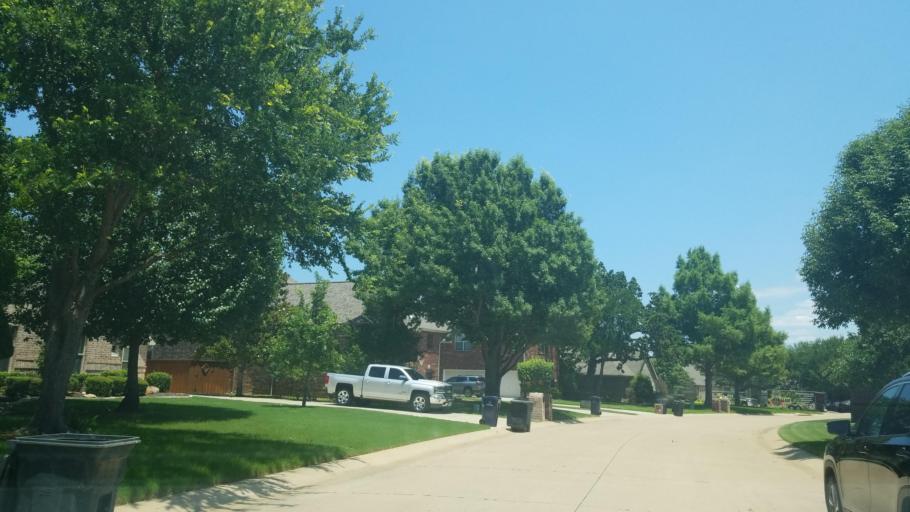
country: US
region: Texas
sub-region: Denton County
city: Copper Canyon
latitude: 33.0794
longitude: -97.0807
